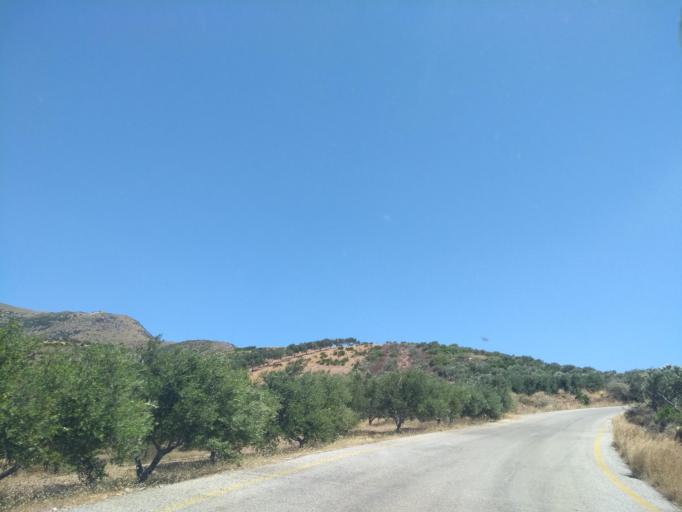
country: GR
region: Crete
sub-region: Nomos Chanias
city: Vryses
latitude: 35.3603
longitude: 23.5418
